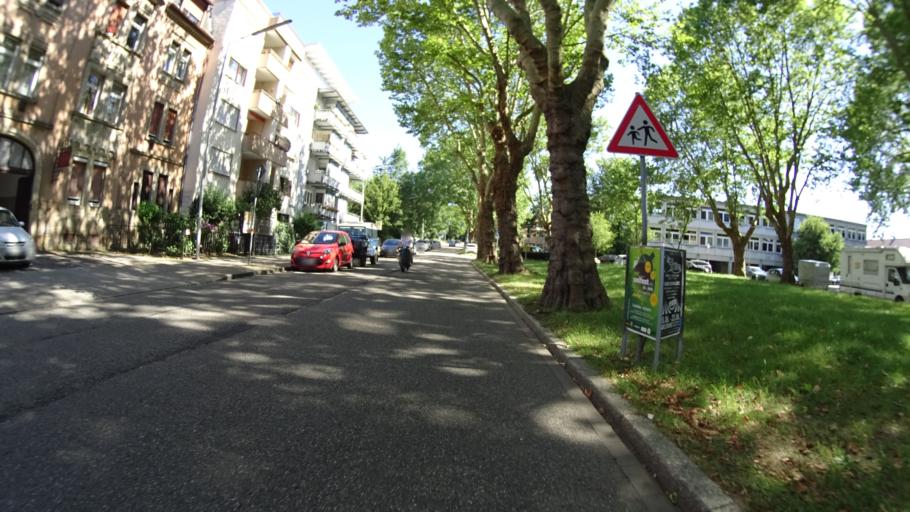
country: DE
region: Baden-Wuerttemberg
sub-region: Karlsruhe Region
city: Weingarten
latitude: 49.0047
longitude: 8.4781
